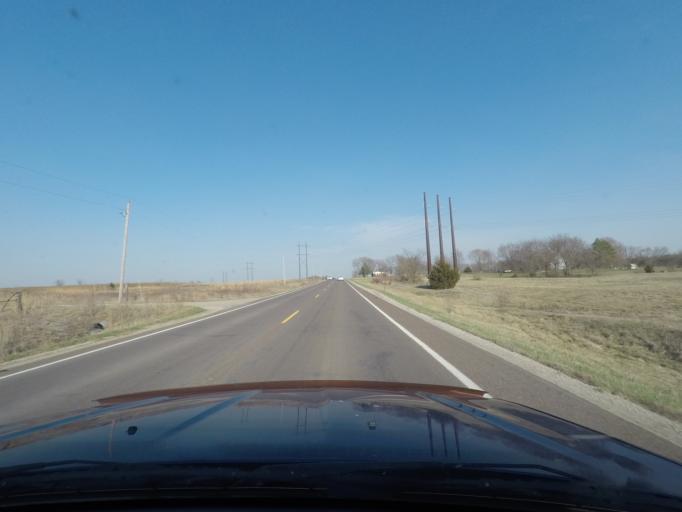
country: US
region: Kansas
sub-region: Douglas County
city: Lawrence
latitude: 39.0006
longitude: -95.3313
